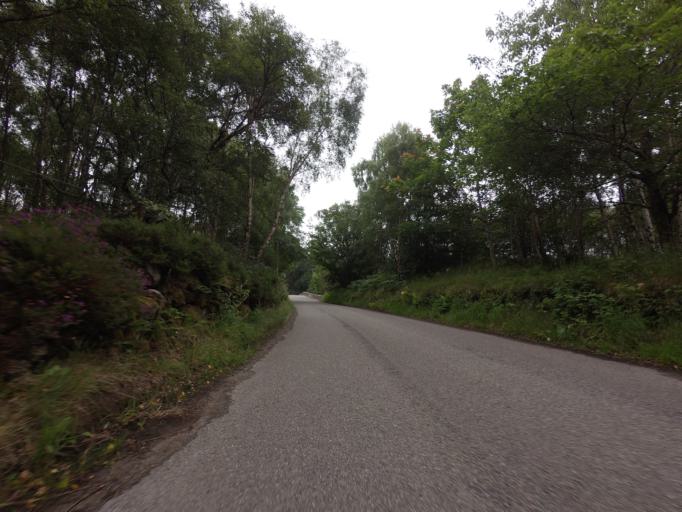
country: GB
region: Scotland
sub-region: Highland
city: Evanton
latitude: 57.8866
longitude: -4.3881
